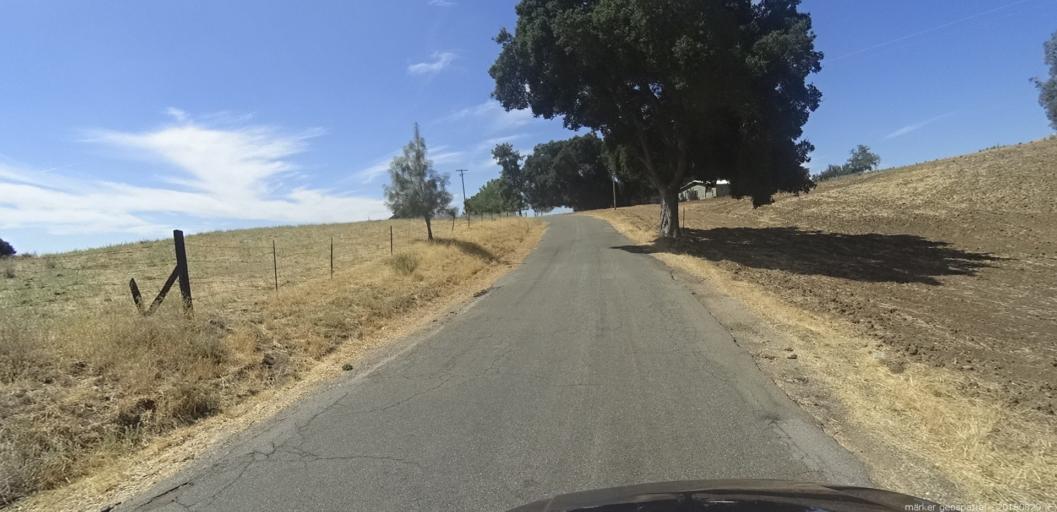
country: US
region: California
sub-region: San Luis Obispo County
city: Lake Nacimiento
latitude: 35.8181
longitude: -121.0573
